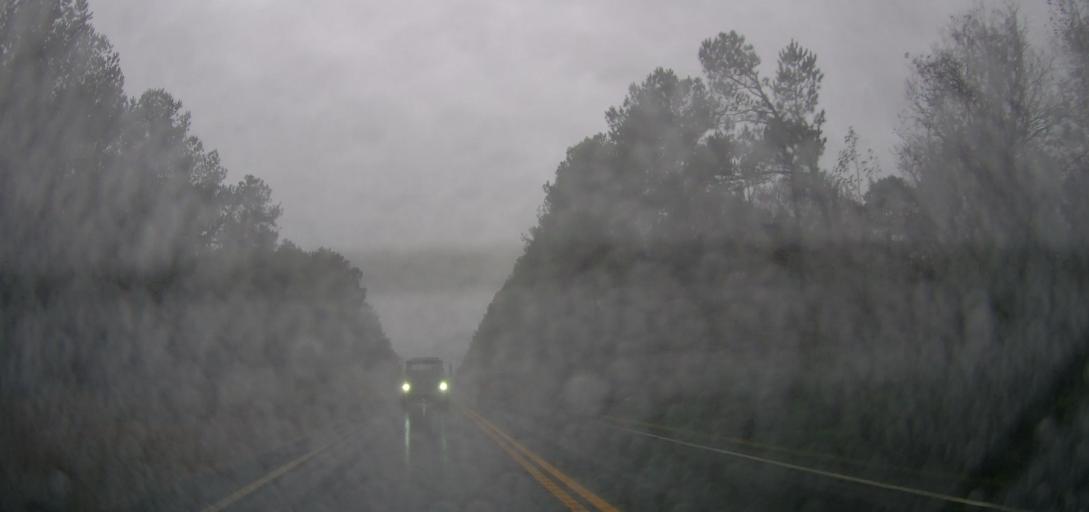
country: US
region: Georgia
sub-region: Putnam County
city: Eatonton
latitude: 33.1945
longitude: -83.4340
